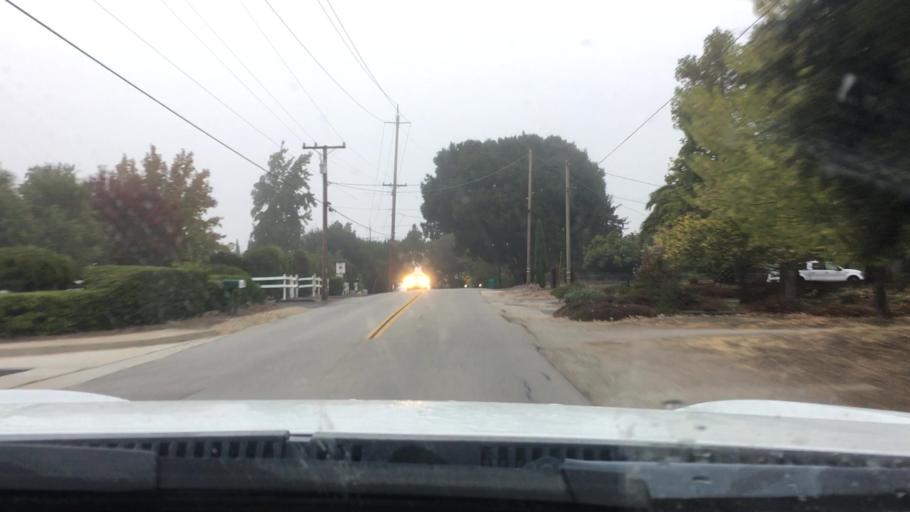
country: US
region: California
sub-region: San Luis Obispo County
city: Atascadero
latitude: 35.4887
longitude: -120.6866
